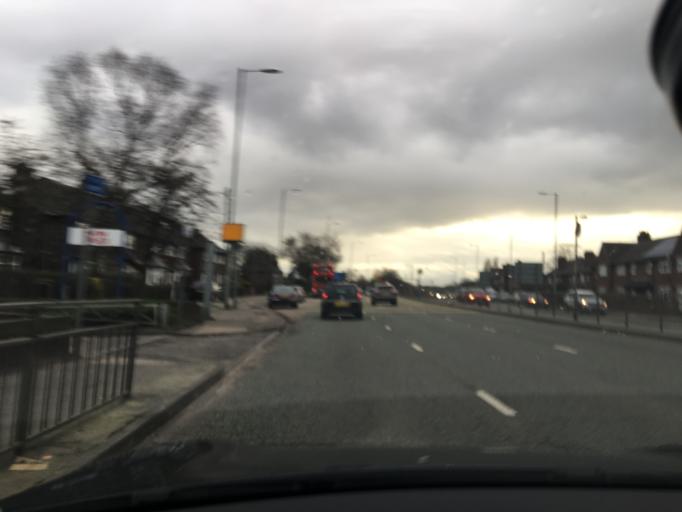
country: GB
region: England
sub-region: Manchester
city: Chorlton cum Hardy
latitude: 53.4223
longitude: -2.2582
